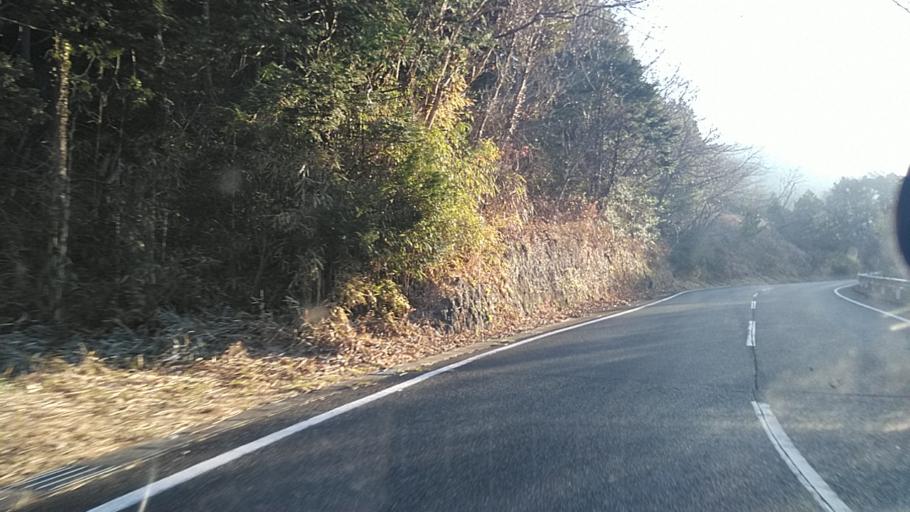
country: JP
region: Chiba
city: Kimitsu
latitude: 35.2587
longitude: 139.9358
